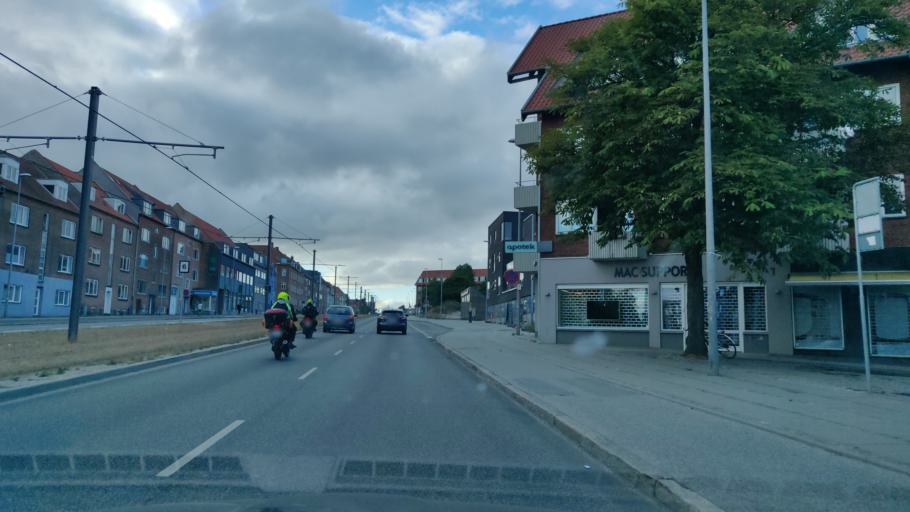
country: DK
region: Central Jutland
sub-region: Arhus Kommune
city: Arhus
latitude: 56.1744
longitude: 10.2030
